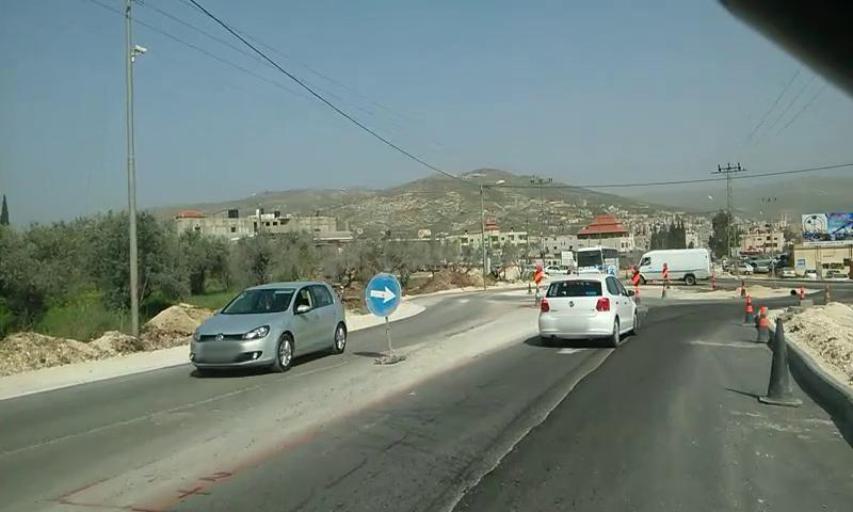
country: PS
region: West Bank
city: Huwwarah
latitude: 32.1369
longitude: 35.2581
